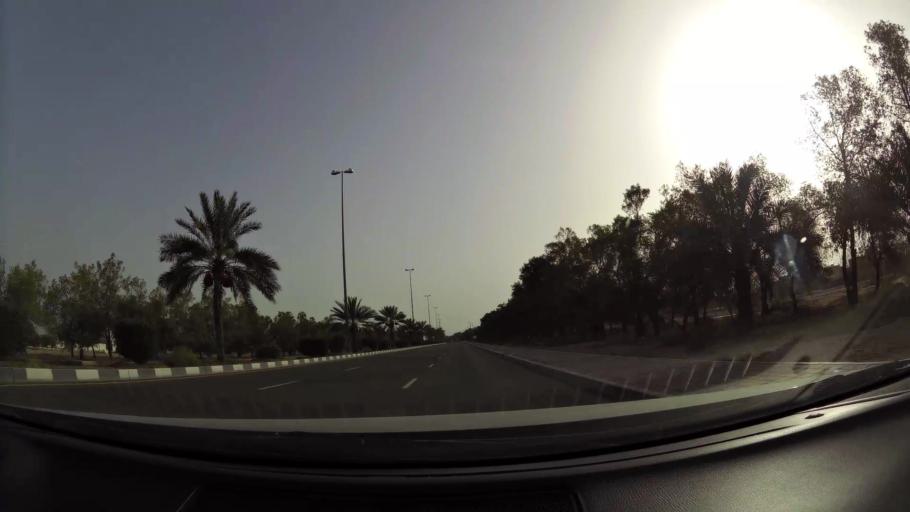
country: AE
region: Abu Dhabi
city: Al Ain
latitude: 24.1174
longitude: 55.7029
